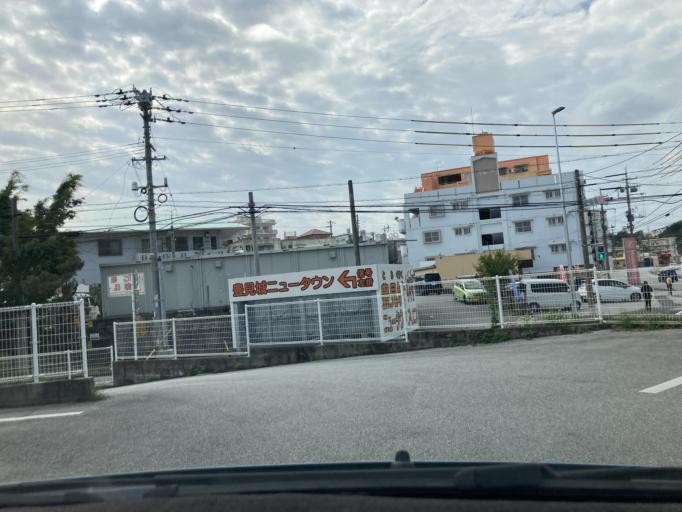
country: JP
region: Okinawa
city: Tomigusuku
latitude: 26.1909
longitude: 127.6926
